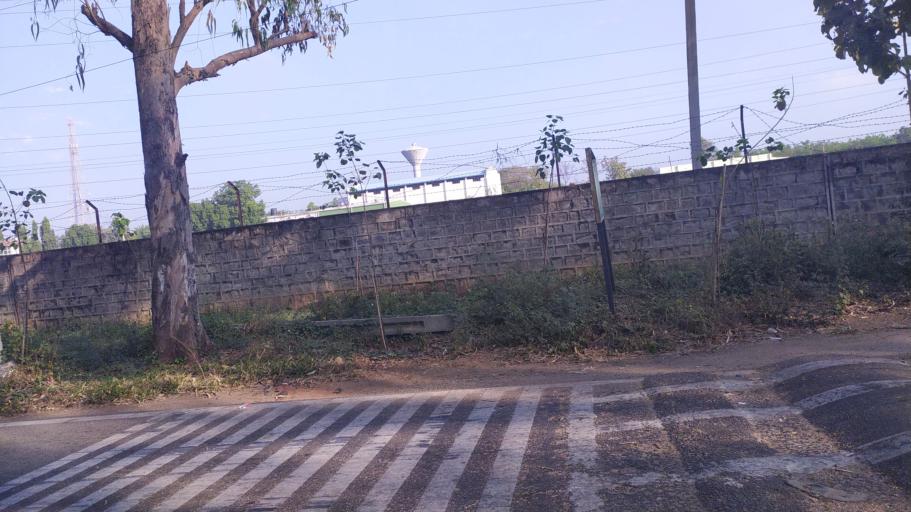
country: IN
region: Telangana
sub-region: Hyderabad
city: Hyderabad
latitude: 17.3297
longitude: 78.4111
